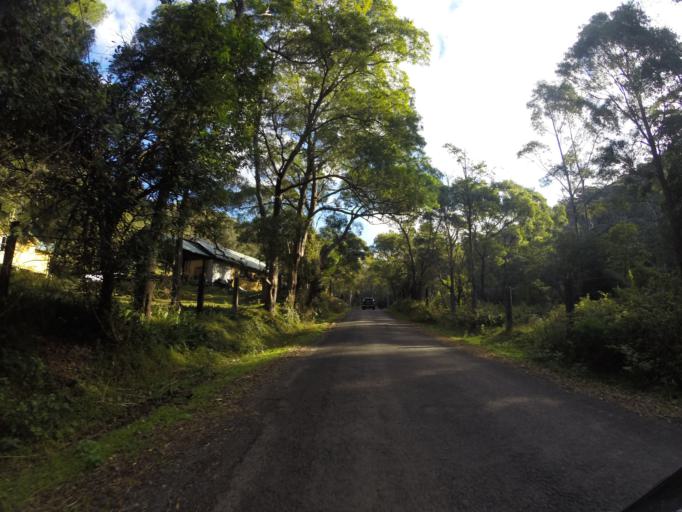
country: AU
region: New South Wales
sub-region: Wollongong
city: Cordeaux Heights
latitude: -34.4366
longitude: 150.7990
